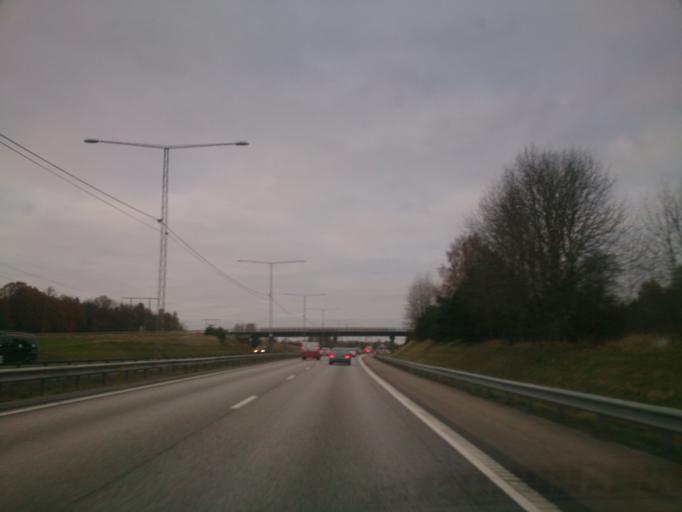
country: SE
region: Stockholm
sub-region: Sigtuna Kommun
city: Rosersberg
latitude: 59.5915
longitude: 17.8970
